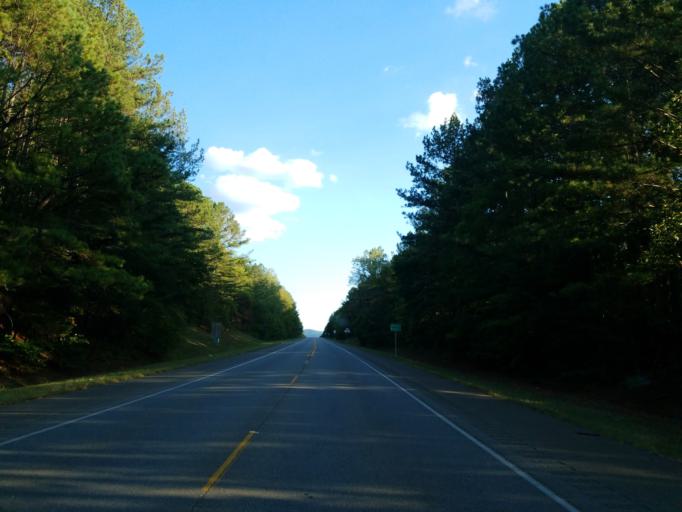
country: US
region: Georgia
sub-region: Murray County
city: Chatsworth
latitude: 34.5991
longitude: -84.7108
